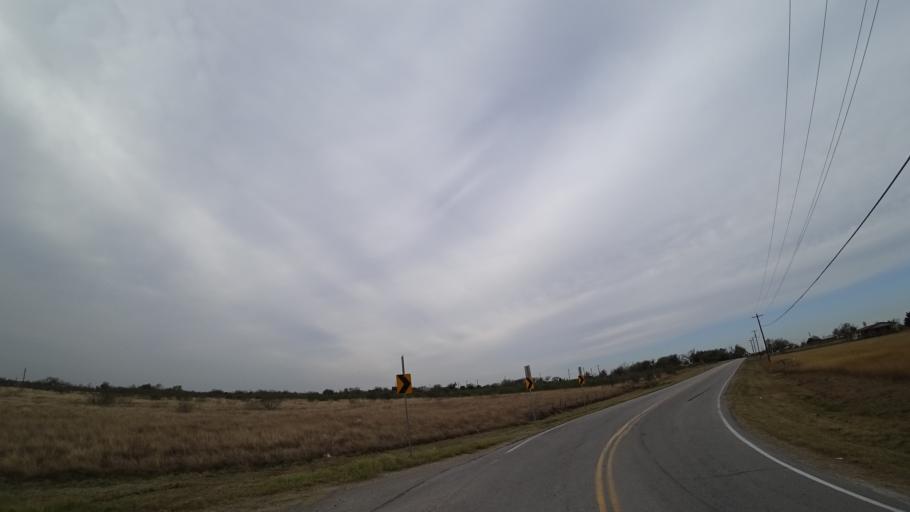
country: US
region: Texas
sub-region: Travis County
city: Garfield
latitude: 30.1221
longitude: -97.6292
